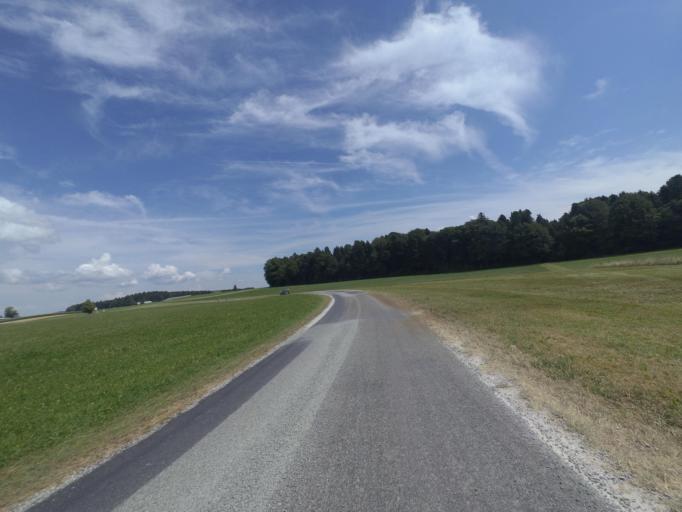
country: AT
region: Salzburg
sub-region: Politischer Bezirk Salzburg-Umgebung
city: Elixhausen
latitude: 47.8975
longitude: 13.0898
